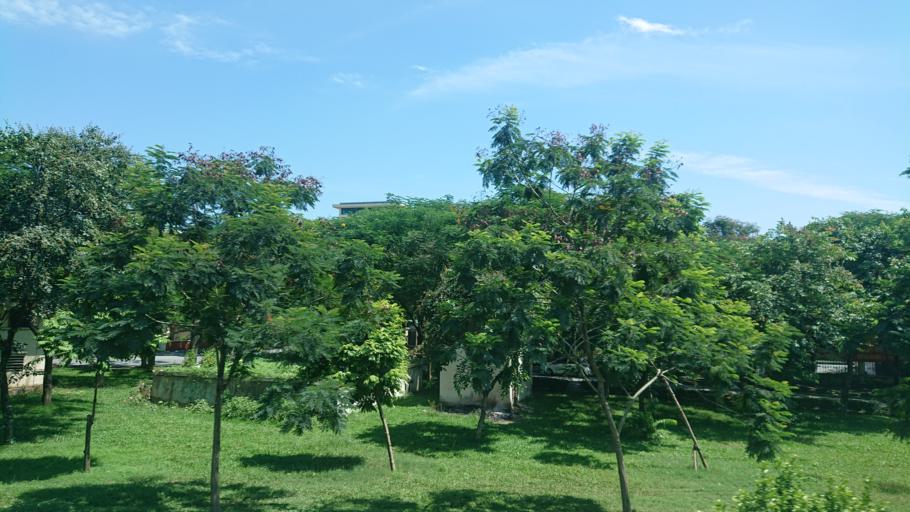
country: VN
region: Ha Noi
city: Van Dien
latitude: 20.9670
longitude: 105.8476
